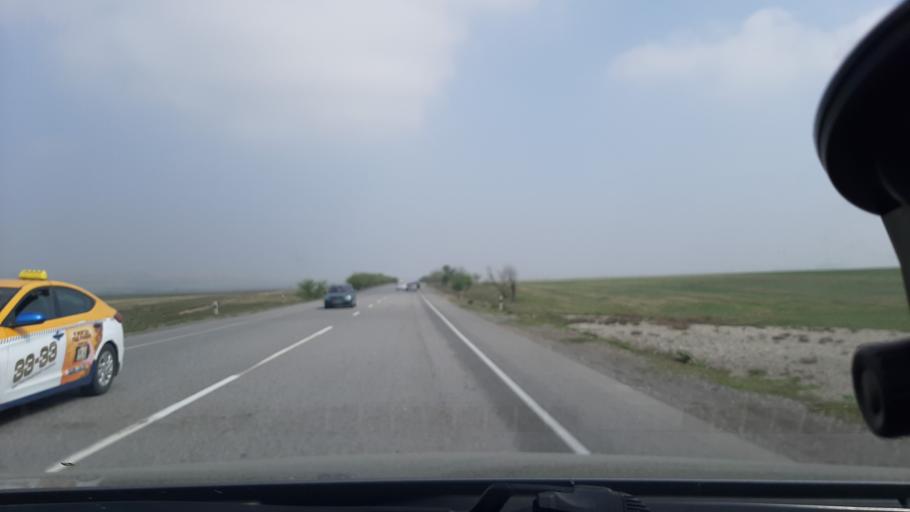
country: UZ
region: Toshkent
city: Bekobod
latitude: 40.1090
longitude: 69.1885
